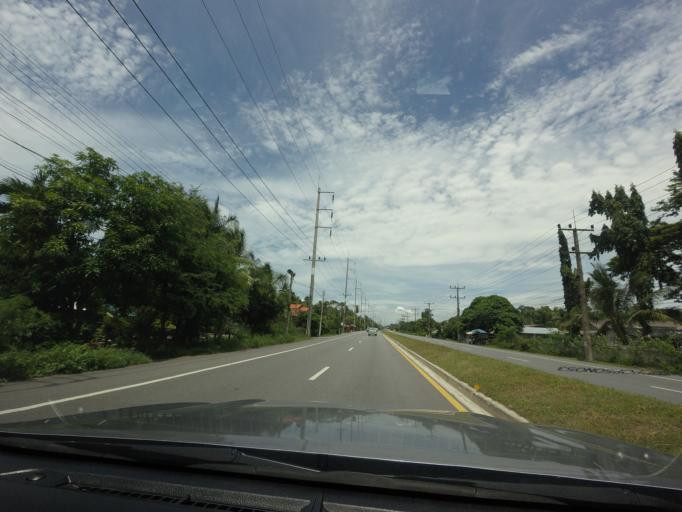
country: TH
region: Songkhla
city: Krasae Sin
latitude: 7.5866
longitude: 100.4054
